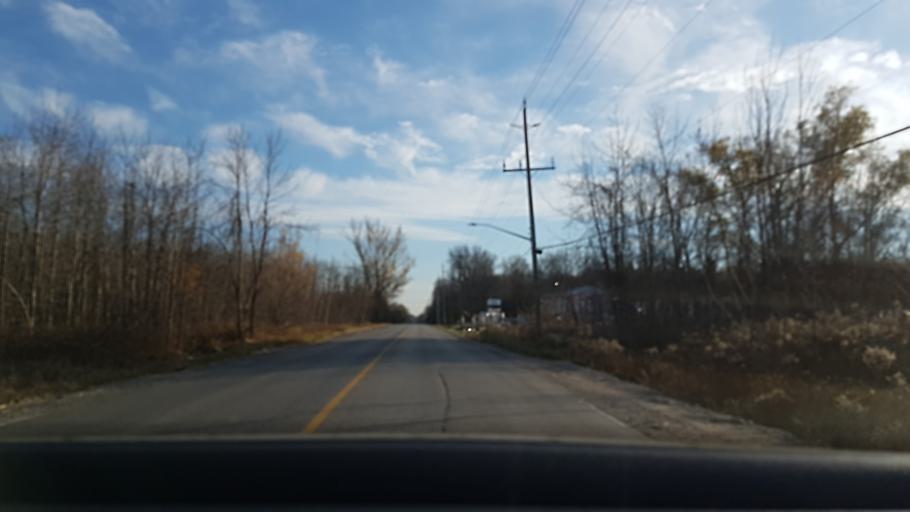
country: CA
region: Ontario
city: Innisfil
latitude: 44.3490
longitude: -79.5480
